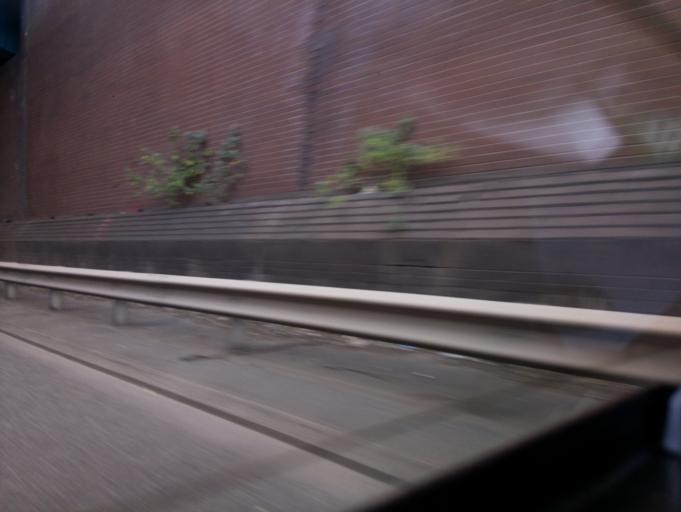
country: GB
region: England
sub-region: Coventry
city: Coventry
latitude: 52.4145
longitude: -1.4870
